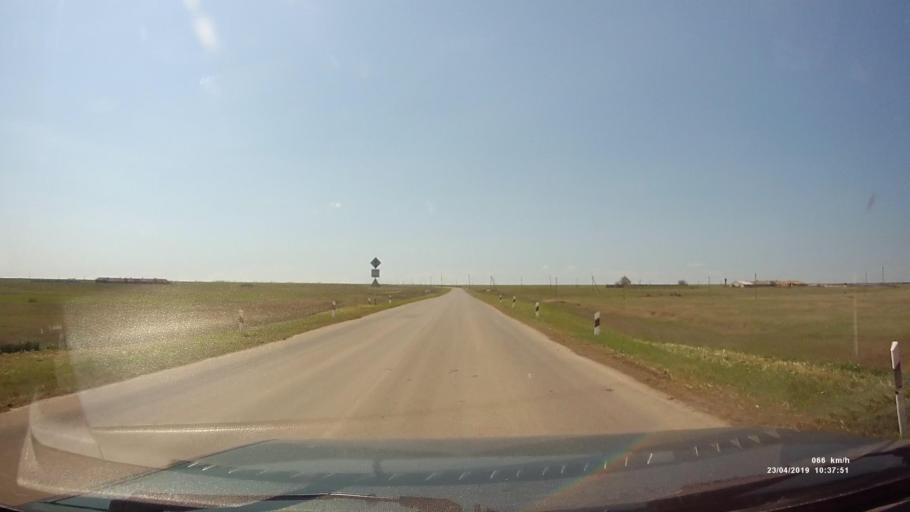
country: RU
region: Kalmykiya
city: Yashalta
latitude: 46.5393
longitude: 42.6400
